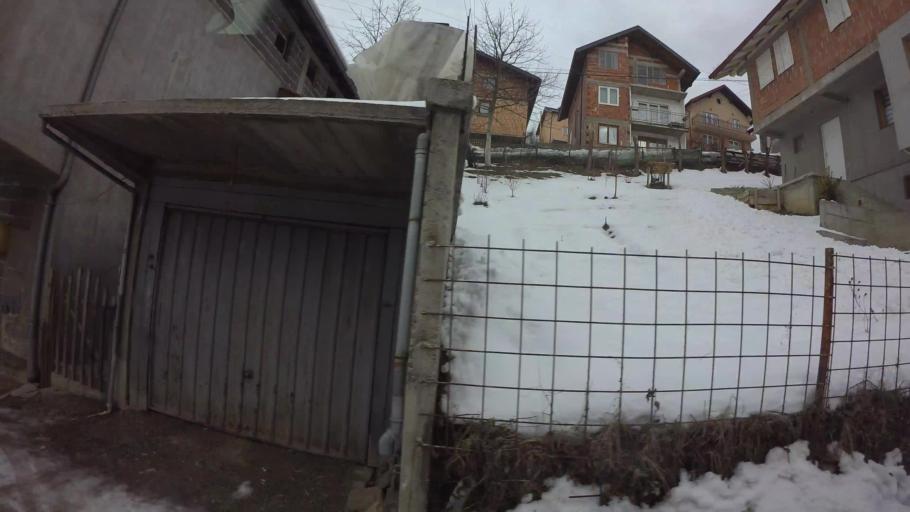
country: BA
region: Federation of Bosnia and Herzegovina
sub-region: Kanton Sarajevo
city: Sarajevo
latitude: 43.8598
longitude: 18.3335
